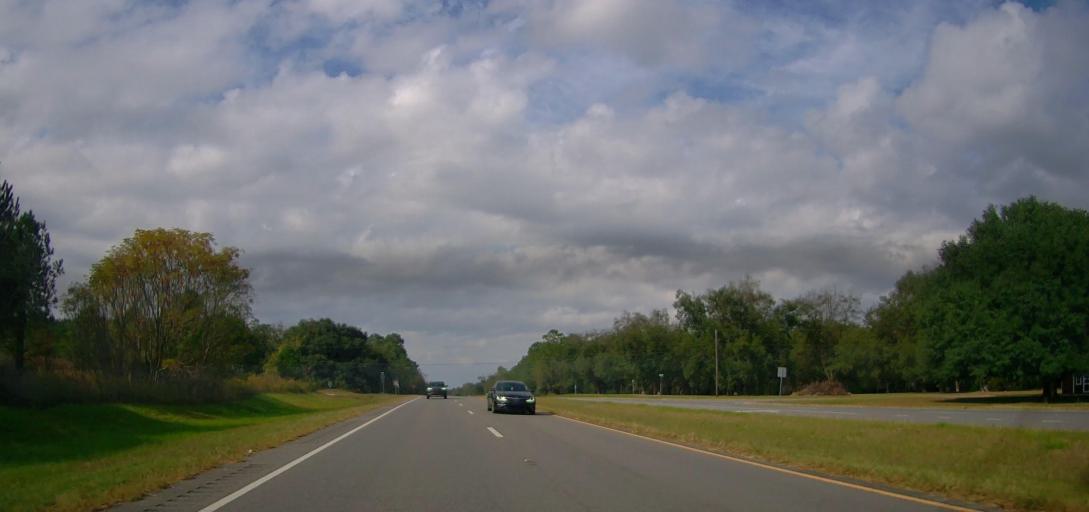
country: US
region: Georgia
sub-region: Thomas County
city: Meigs
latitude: 31.0083
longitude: -84.0519
